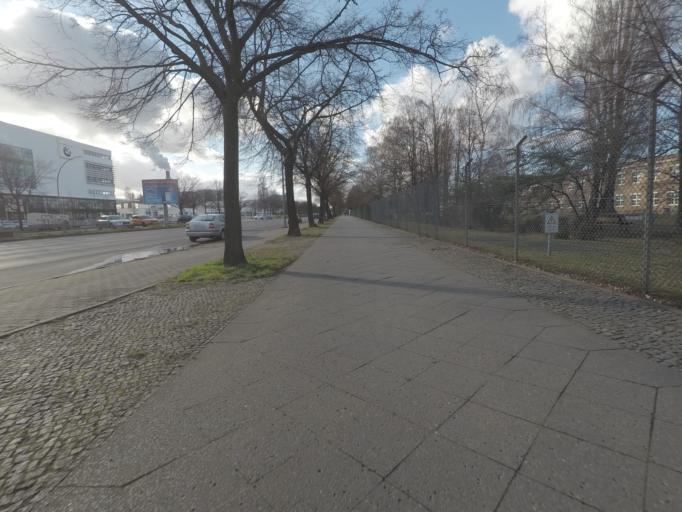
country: DE
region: Berlin
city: Siemensstadt
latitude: 52.5375
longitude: 13.2585
